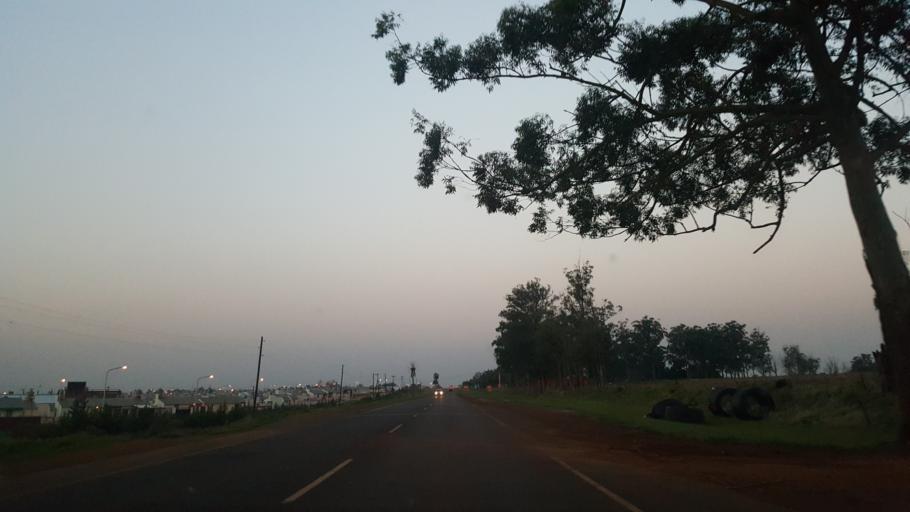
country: AR
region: Misiones
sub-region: Departamento de Capital
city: Posadas
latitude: -27.4154
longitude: -55.9856
